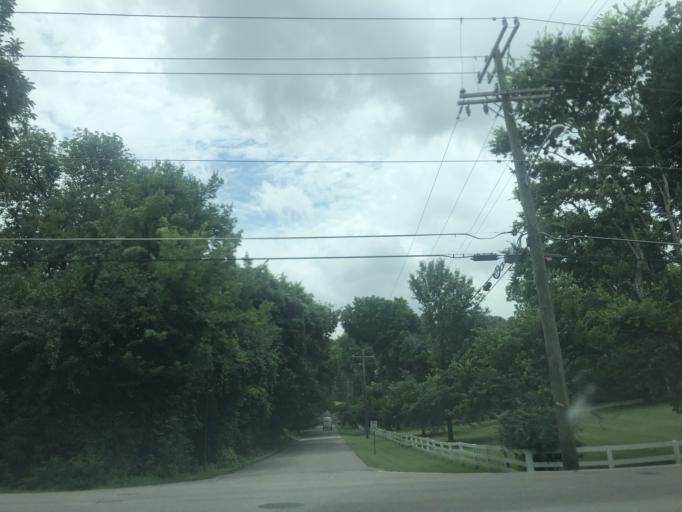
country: US
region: Tennessee
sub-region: Davidson County
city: Oak Hill
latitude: 36.0809
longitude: -86.7991
